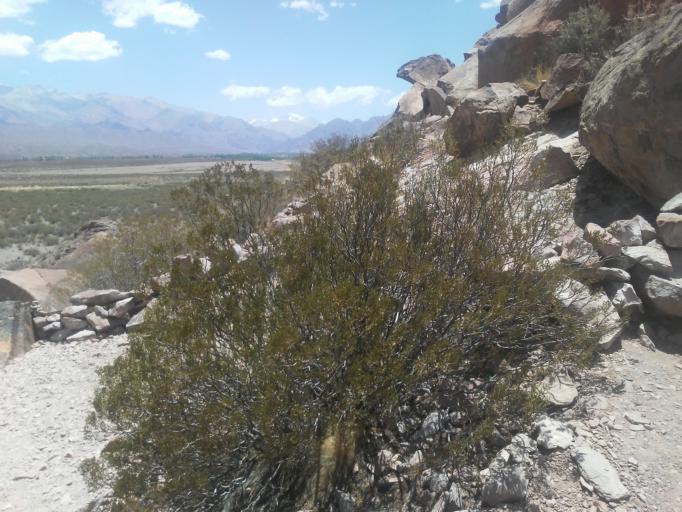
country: AR
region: Mendoza
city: Las Heras
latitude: -32.5306
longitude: -69.3133
